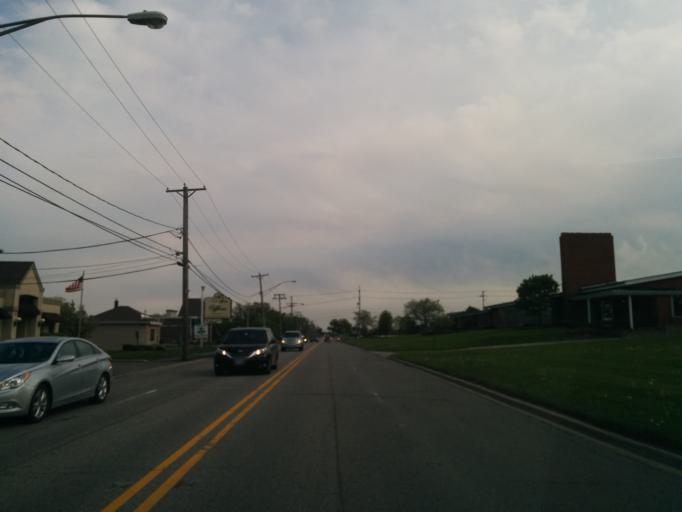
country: US
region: Illinois
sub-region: Kane County
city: North Aurora
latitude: 41.8013
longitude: -88.3257
